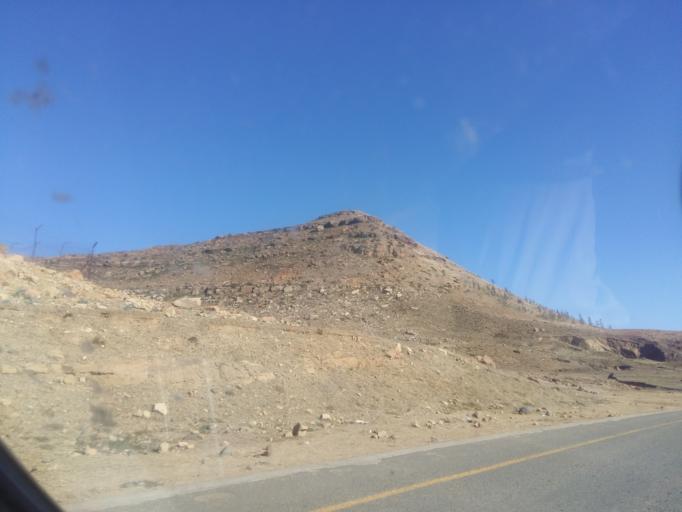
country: LS
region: Mafeteng
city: Mafeteng
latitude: -29.6931
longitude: 27.2802
